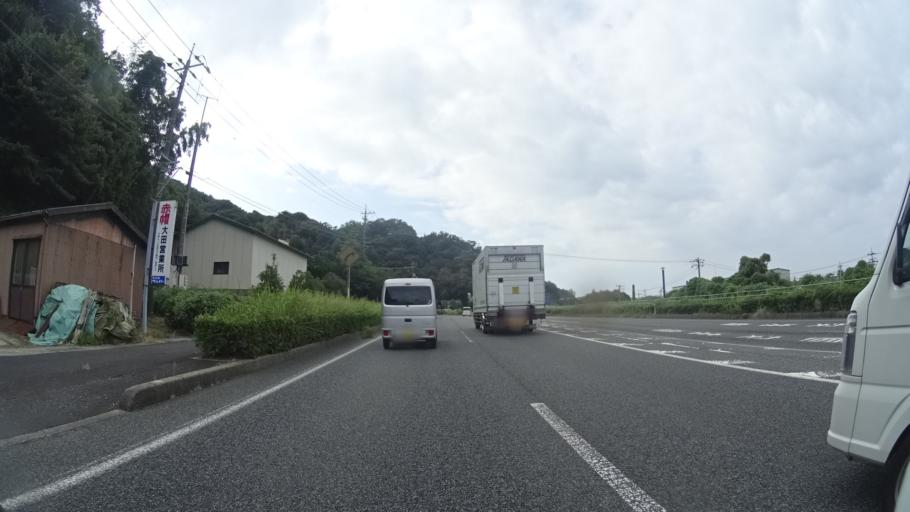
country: JP
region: Shimane
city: Odacho-oda
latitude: 35.2084
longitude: 132.5040
